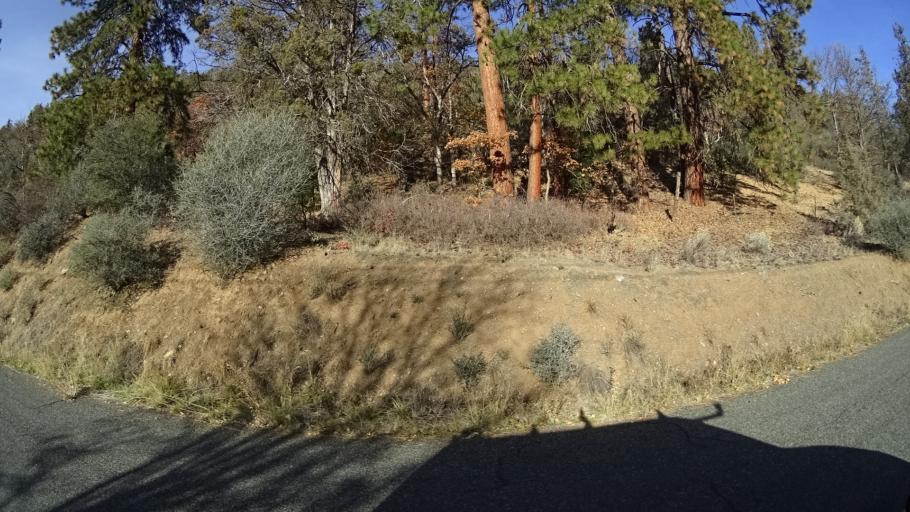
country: US
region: California
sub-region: Siskiyou County
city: Yreka
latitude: 41.6534
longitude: -122.6293
